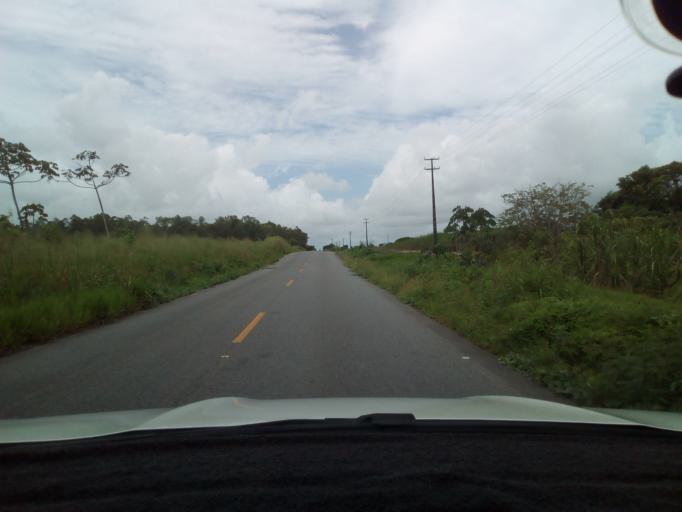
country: BR
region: Paraiba
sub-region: Conde
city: Conde
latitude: -7.3442
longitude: -34.9767
